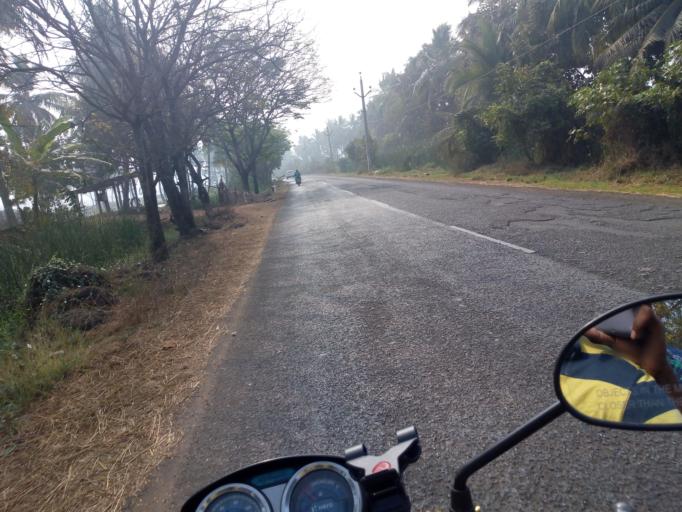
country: IN
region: Andhra Pradesh
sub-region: West Godavari
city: Tadepallegudem
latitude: 16.7959
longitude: 81.4154
